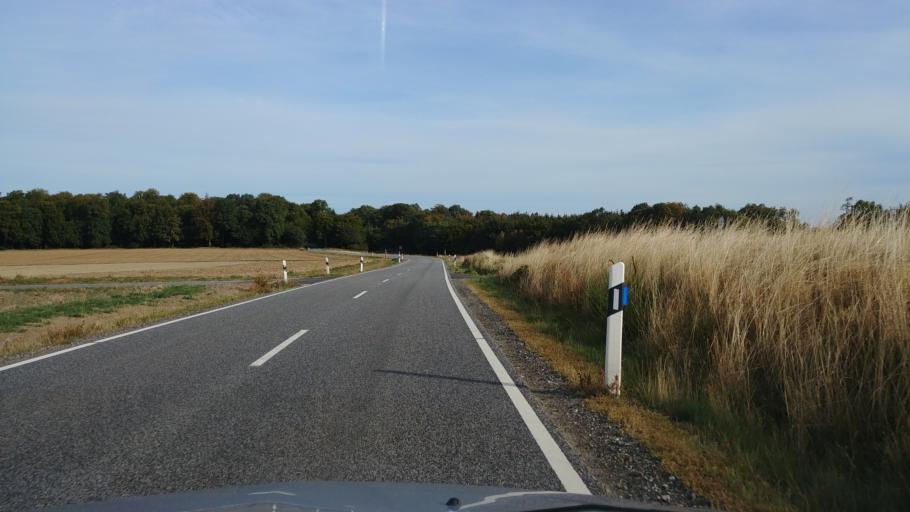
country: DE
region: Rheinland-Pfalz
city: Reckenroth
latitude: 50.1919
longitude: 8.0105
